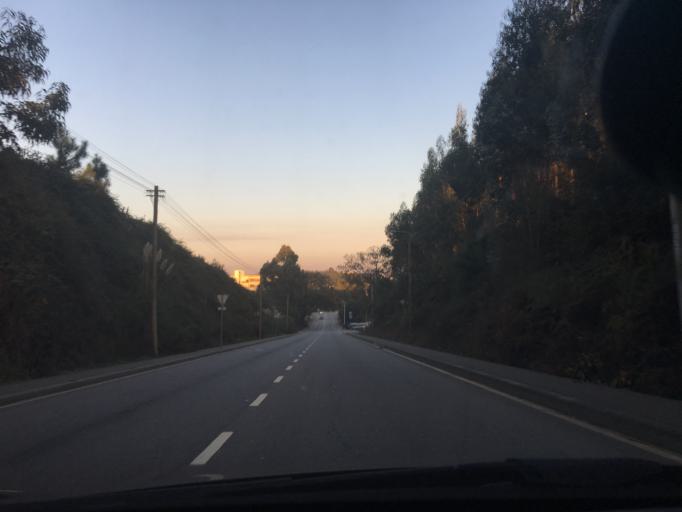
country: PT
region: Porto
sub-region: Maia
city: Gemunde
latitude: 41.2399
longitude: -8.6542
